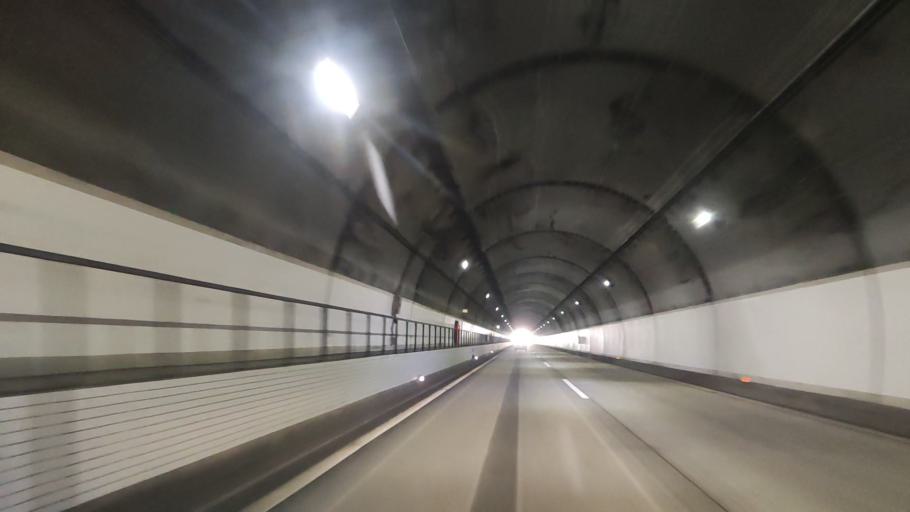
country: JP
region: Ehime
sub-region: Shikoku-chuo Shi
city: Matsuyama
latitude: 33.8213
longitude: 132.9664
